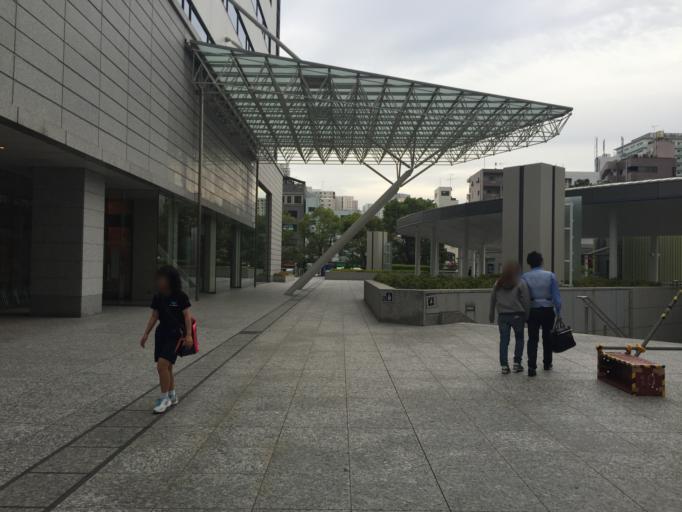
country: JP
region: Tokyo
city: Urayasu
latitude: 35.6560
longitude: 139.7967
